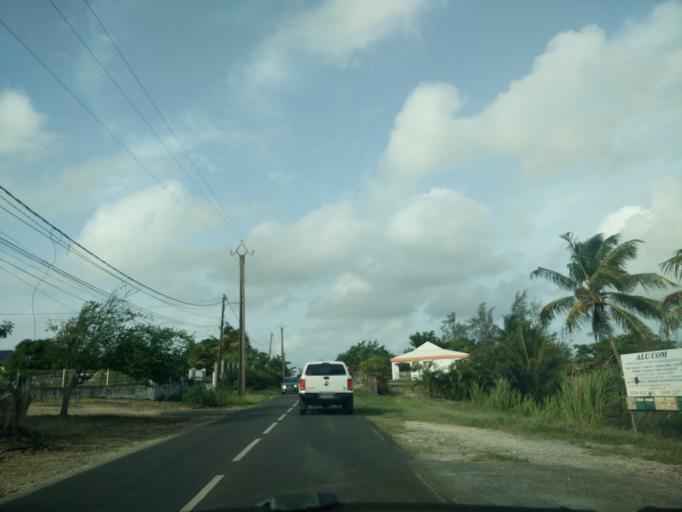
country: GP
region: Guadeloupe
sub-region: Guadeloupe
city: Sainte-Anne
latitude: 16.2796
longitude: -61.3751
